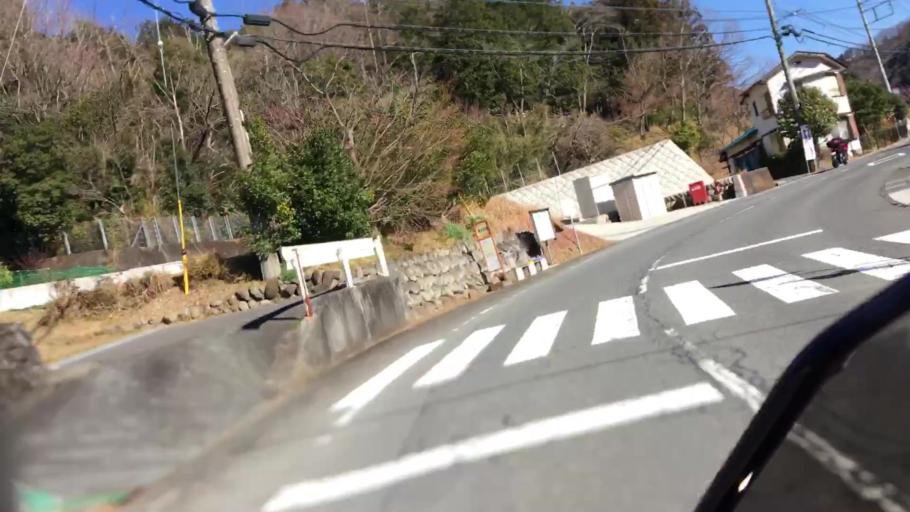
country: JP
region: Shizuoka
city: Ito
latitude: 34.9822
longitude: 138.9636
